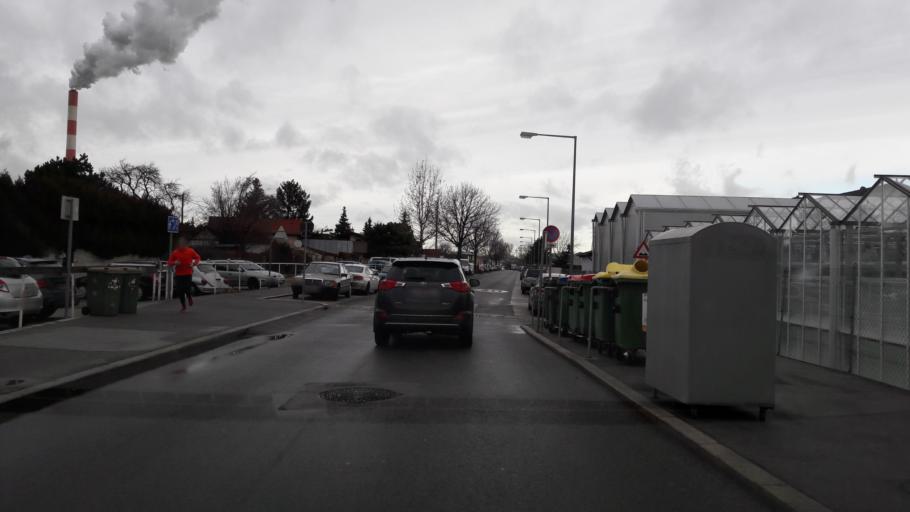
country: AT
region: Lower Austria
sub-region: Politischer Bezirk Wien-Umgebung
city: Schwechat
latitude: 48.1718
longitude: 16.4372
